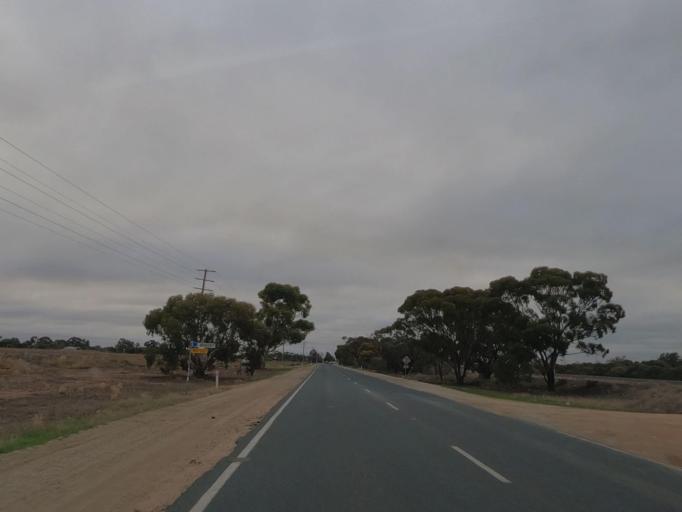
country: AU
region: Victoria
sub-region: Swan Hill
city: Swan Hill
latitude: -35.3930
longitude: 143.5713
